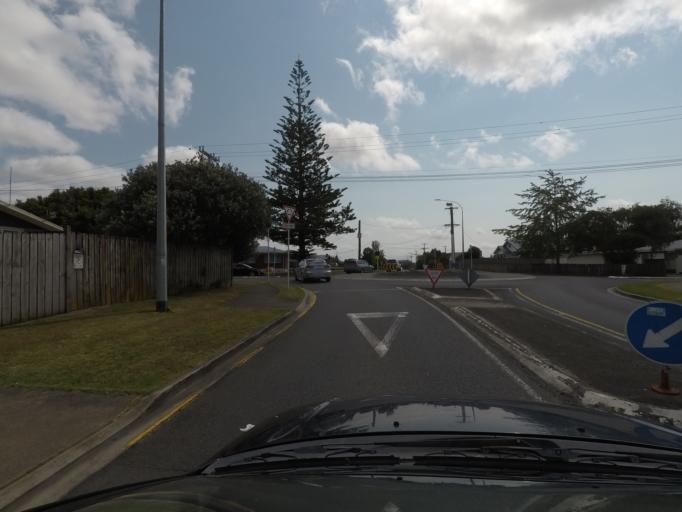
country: NZ
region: Northland
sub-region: Whangarei
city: Whangarei
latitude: -35.6882
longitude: 174.3234
